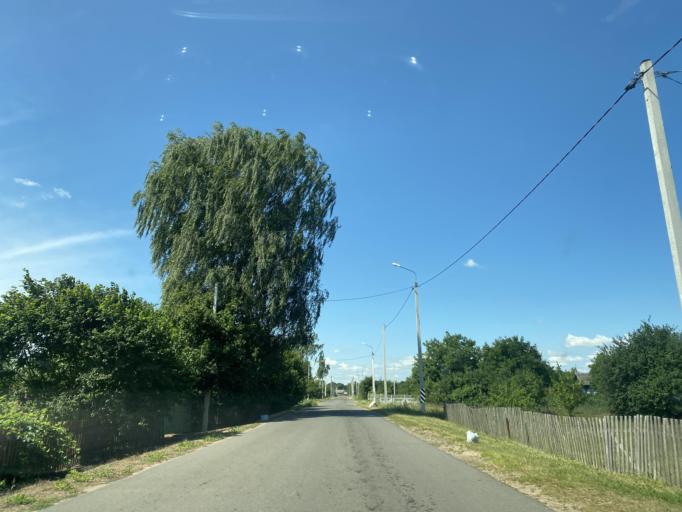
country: BY
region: Brest
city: Ivanava
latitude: 52.1725
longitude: 25.5613
